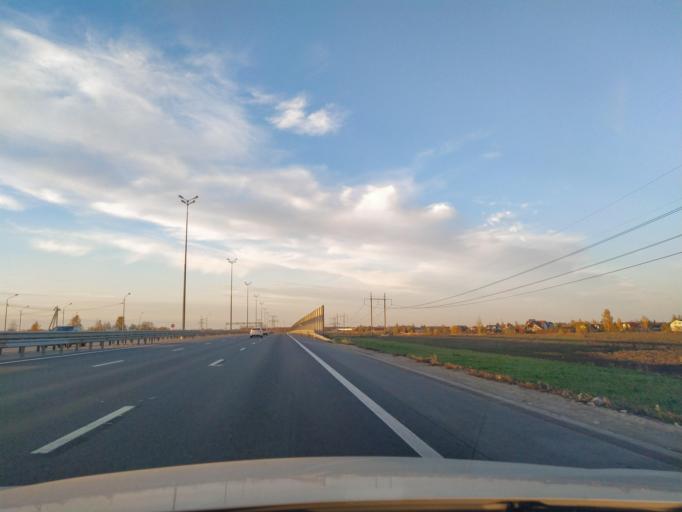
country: RU
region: Leningrad
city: Maloye Verevo
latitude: 59.5918
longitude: 30.1810
